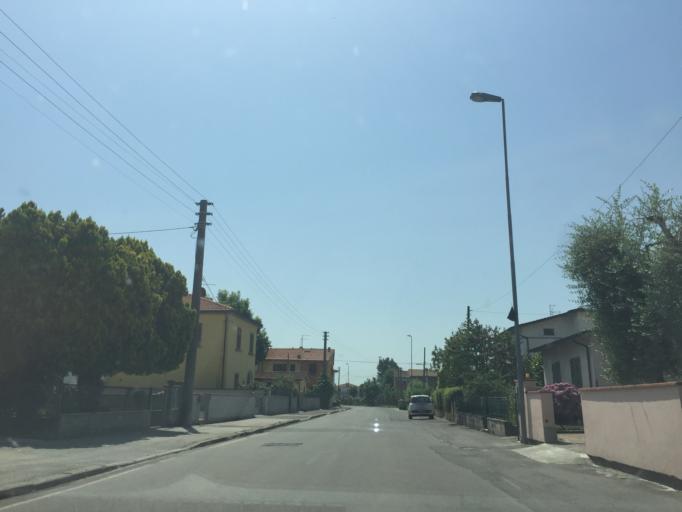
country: IT
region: Tuscany
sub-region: Provincia di Pistoia
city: Anchione
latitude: 43.8248
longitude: 10.7575
